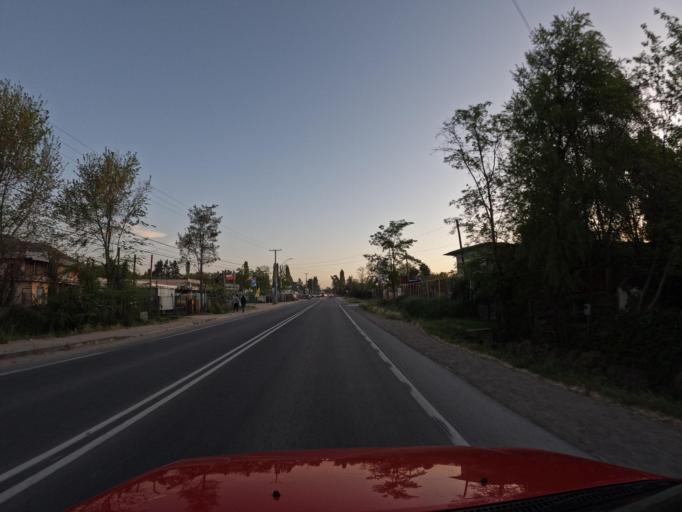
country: CL
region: O'Higgins
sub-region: Provincia de Cachapoal
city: San Vicente
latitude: -34.1730
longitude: -71.3974
